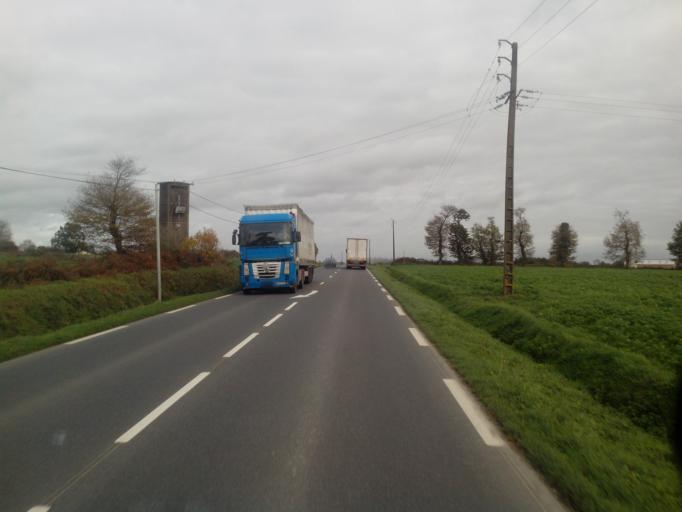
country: FR
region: Brittany
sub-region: Departement d'Ille-et-Vilaine
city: Gael
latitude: 48.1206
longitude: -2.2434
